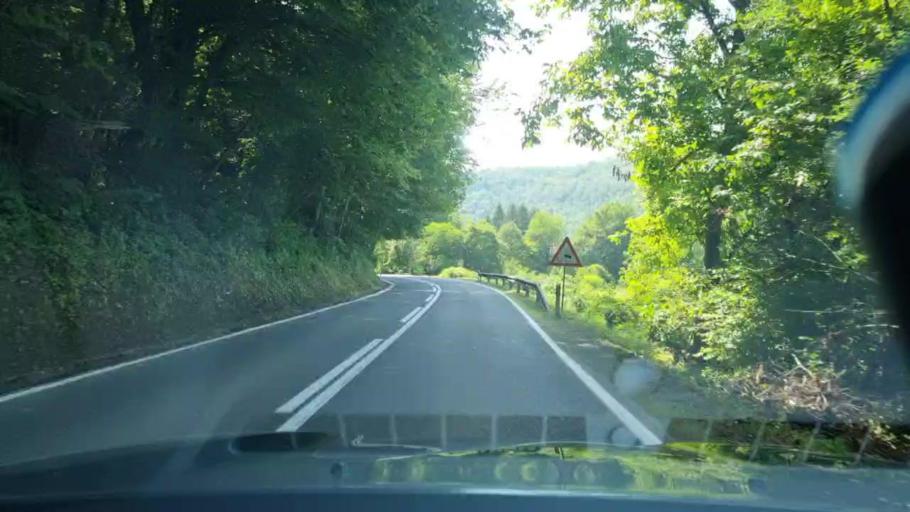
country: BA
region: Federation of Bosnia and Herzegovina
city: Bosanska Krupa
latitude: 44.8777
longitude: 16.1293
